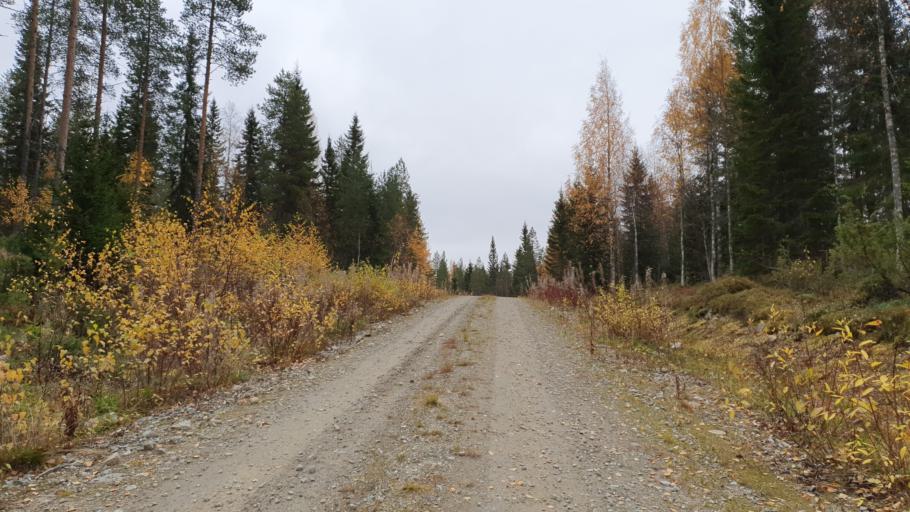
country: FI
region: Kainuu
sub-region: Kehys-Kainuu
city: Kuhmo
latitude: 64.4454
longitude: 29.6263
